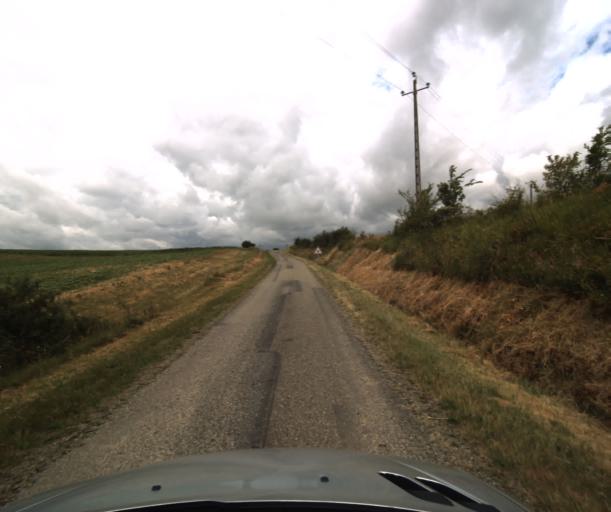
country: FR
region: Midi-Pyrenees
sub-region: Departement du Tarn-et-Garonne
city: Lavit
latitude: 43.9596
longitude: 0.8861
